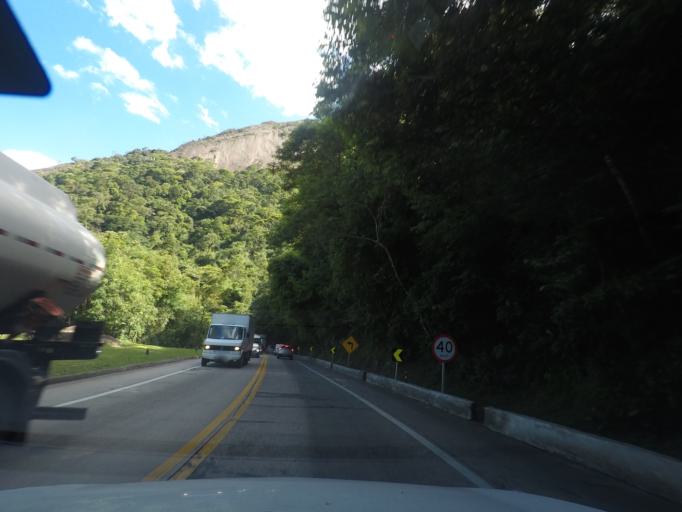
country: BR
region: Rio de Janeiro
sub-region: Teresopolis
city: Teresopolis
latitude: -22.4733
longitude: -43.0013
